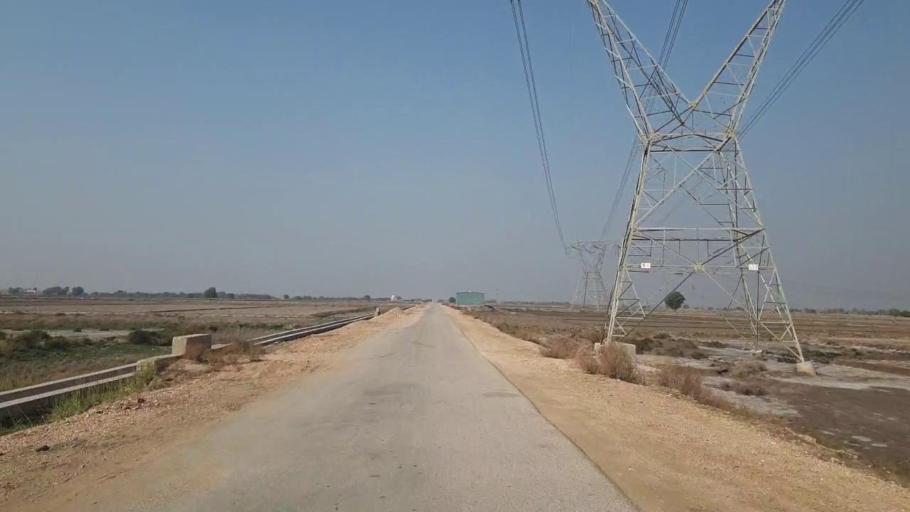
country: PK
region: Sindh
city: Sehwan
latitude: 26.4289
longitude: 67.7675
